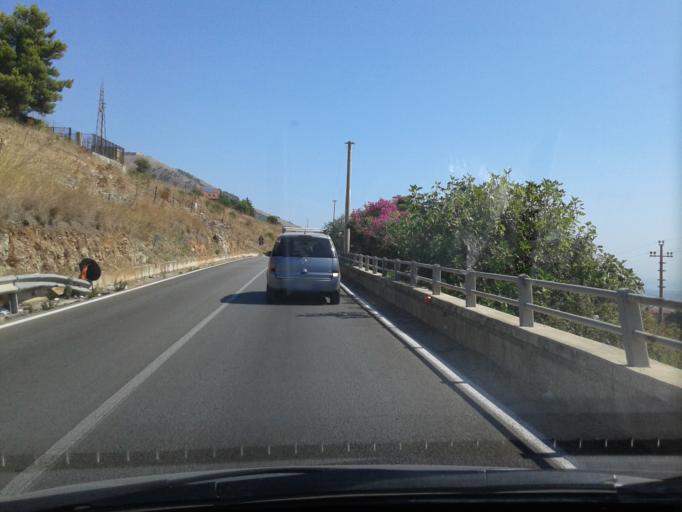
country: IT
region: Sicily
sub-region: Palermo
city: Cannizzaro-Favara
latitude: 38.0617
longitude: 13.2637
